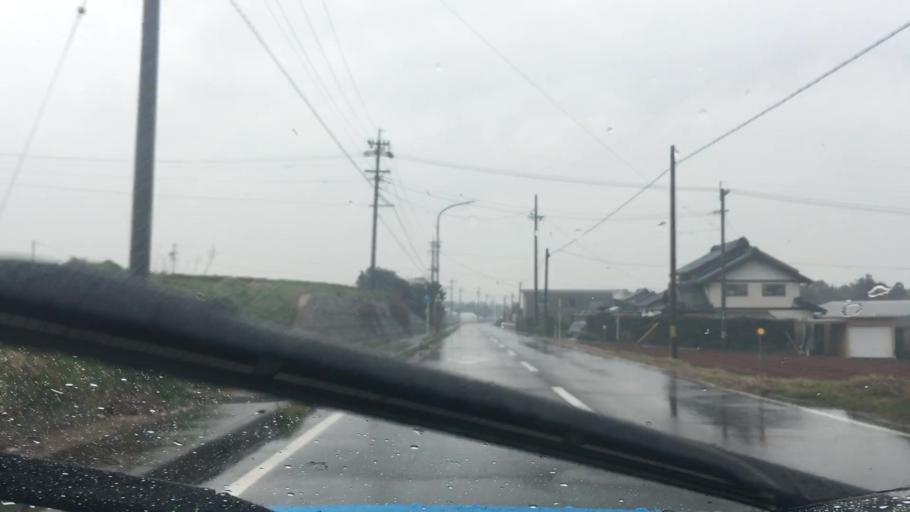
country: JP
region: Aichi
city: Tahara
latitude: 34.6485
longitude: 137.3016
